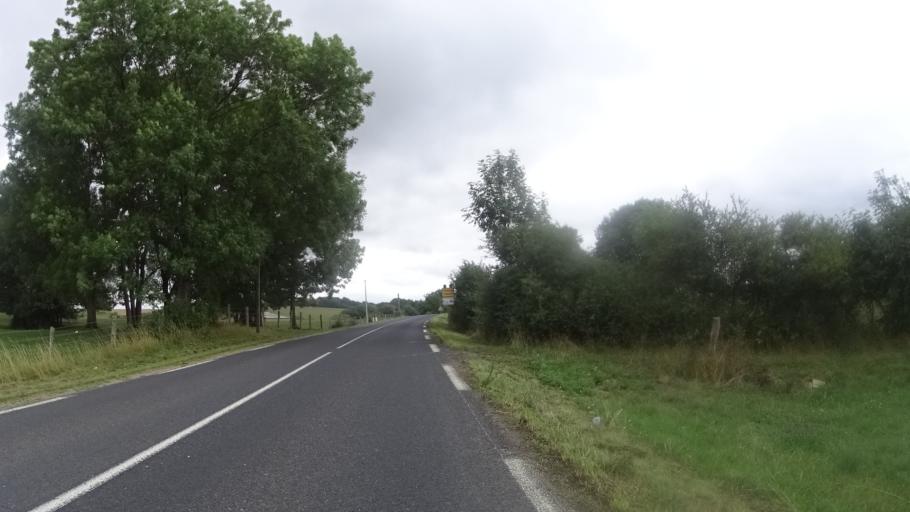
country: FR
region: Lorraine
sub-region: Departement de Meurthe-et-Moselle
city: Art-sur-Meurthe
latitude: 48.6497
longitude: 6.2734
